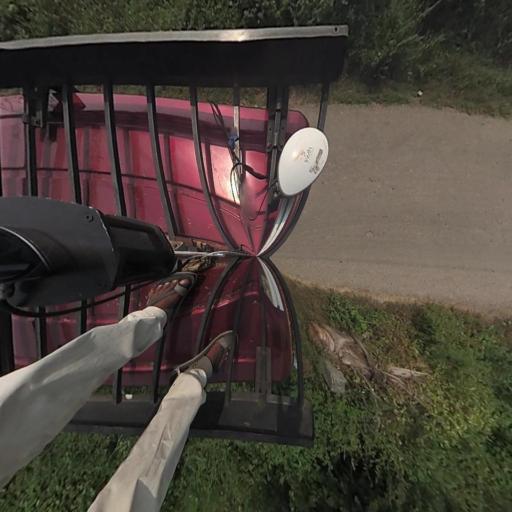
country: IN
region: Telangana
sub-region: Nalgonda
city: Nalgonda
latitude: 17.1820
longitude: 79.1247
